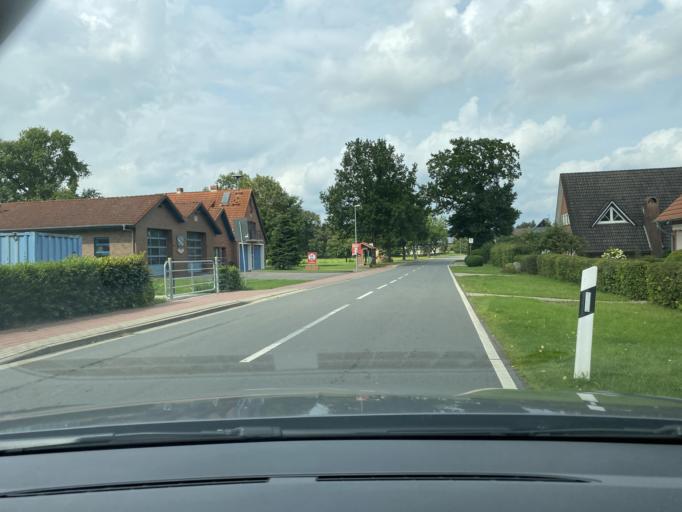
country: DE
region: Lower Saxony
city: Vollersode
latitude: 53.3220
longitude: 8.9102
